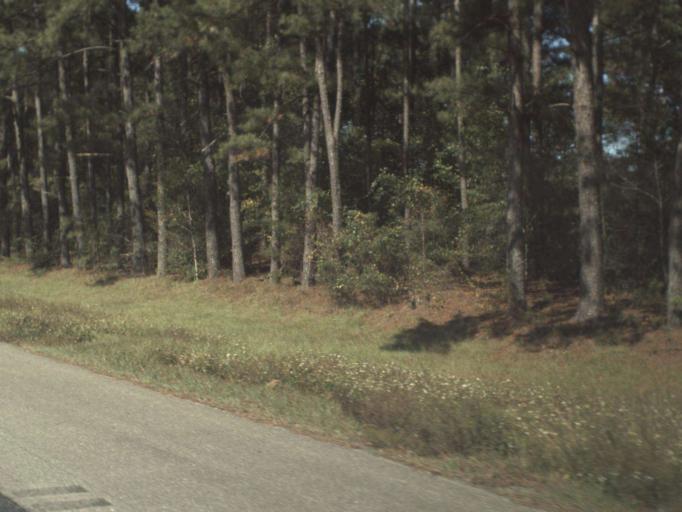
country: US
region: Florida
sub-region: Washington County
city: Chipley
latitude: 30.7454
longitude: -85.4518
